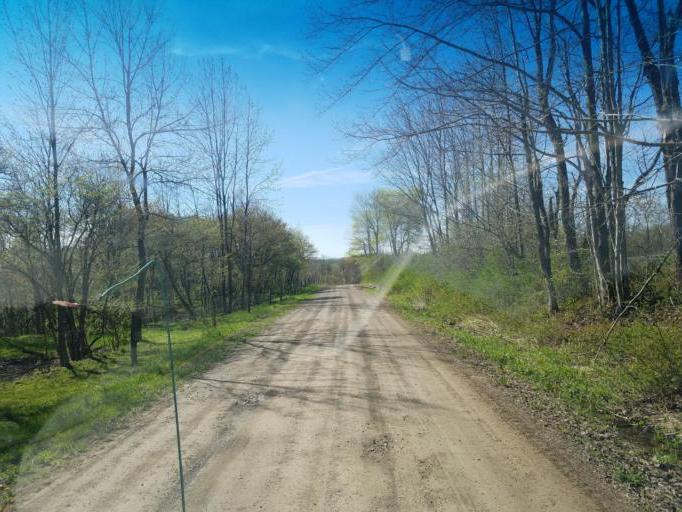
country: US
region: New York
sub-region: Allegany County
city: Andover
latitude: 41.9694
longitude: -77.7841
